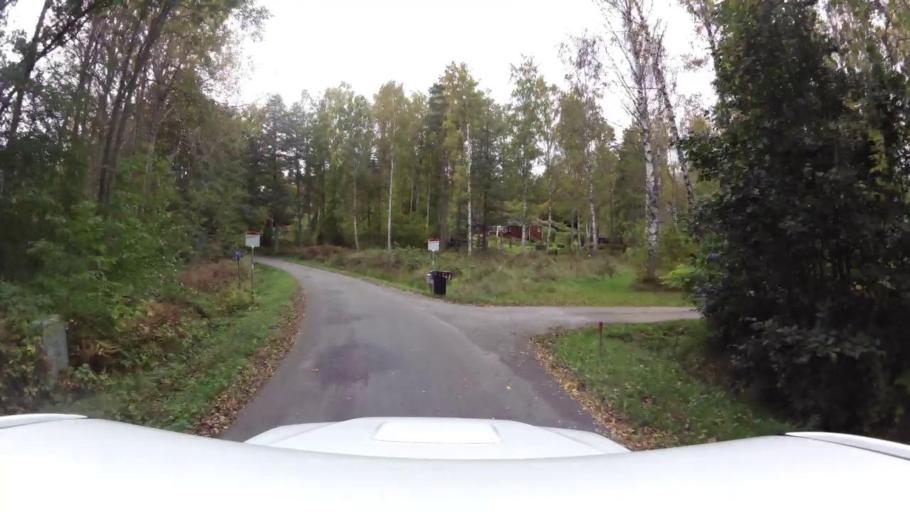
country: SE
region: OEstergoetland
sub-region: Kinda Kommun
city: Rimforsa
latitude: 58.1950
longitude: 15.6036
